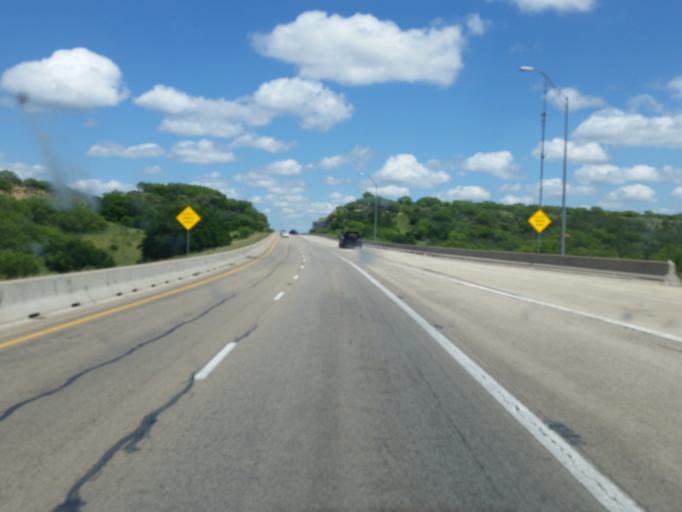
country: US
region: Texas
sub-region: Callahan County
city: Baird
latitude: 32.3961
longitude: -99.3670
